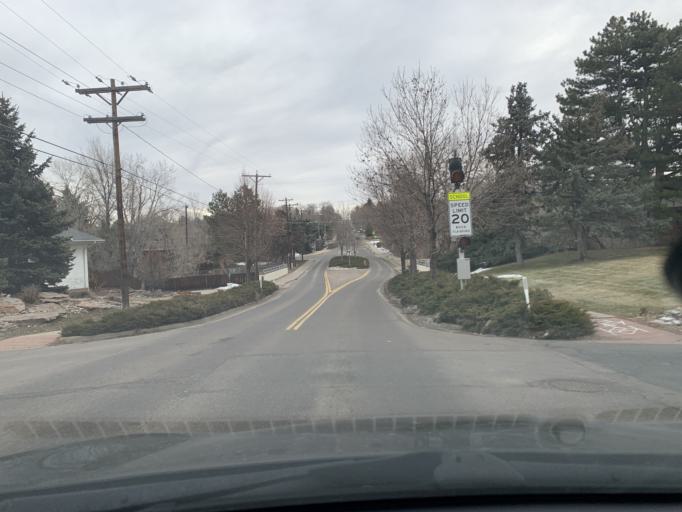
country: US
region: Colorado
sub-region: Jefferson County
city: Applewood
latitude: 39.7473
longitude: -105.1366
